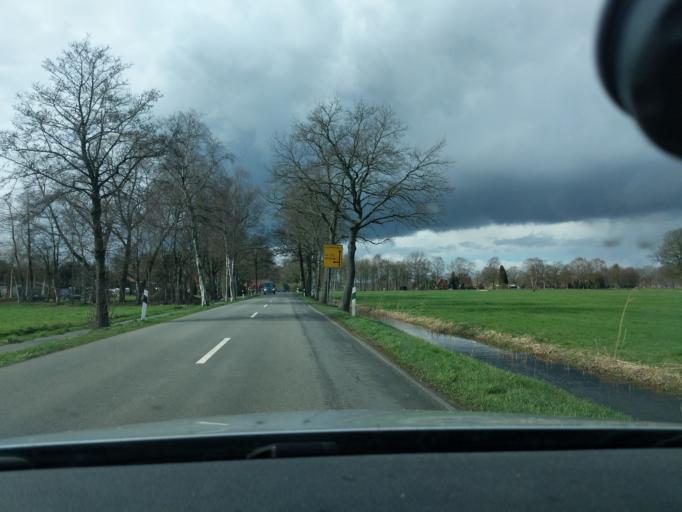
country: DE
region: Lower Saxony
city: Stade
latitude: 53.6256
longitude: 9.4357
